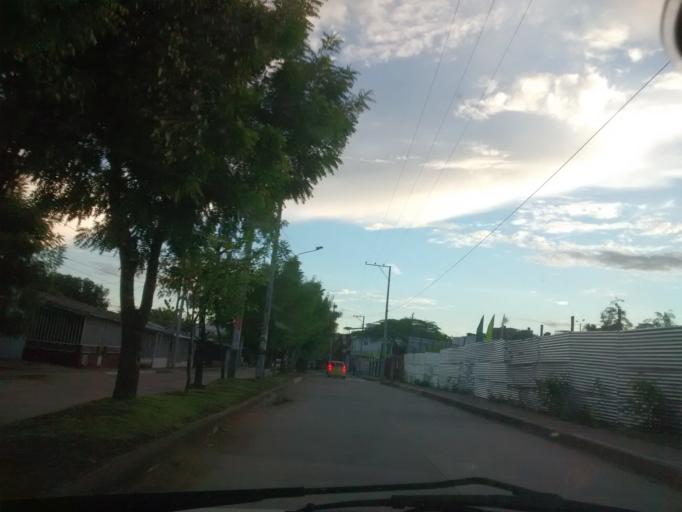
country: CO
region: Cundinamarca
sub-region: Girardot
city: Girardot City
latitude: 4.3157
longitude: -74.7925
